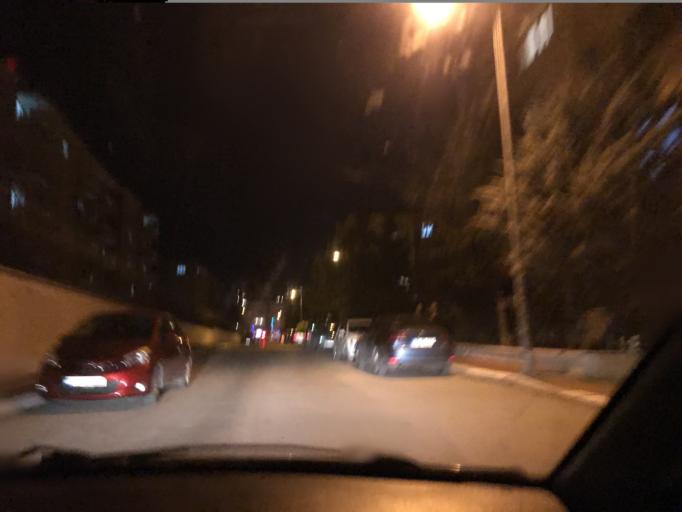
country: TR
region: Ankara
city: Cankaya
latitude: 39.8814
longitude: 32.8749
